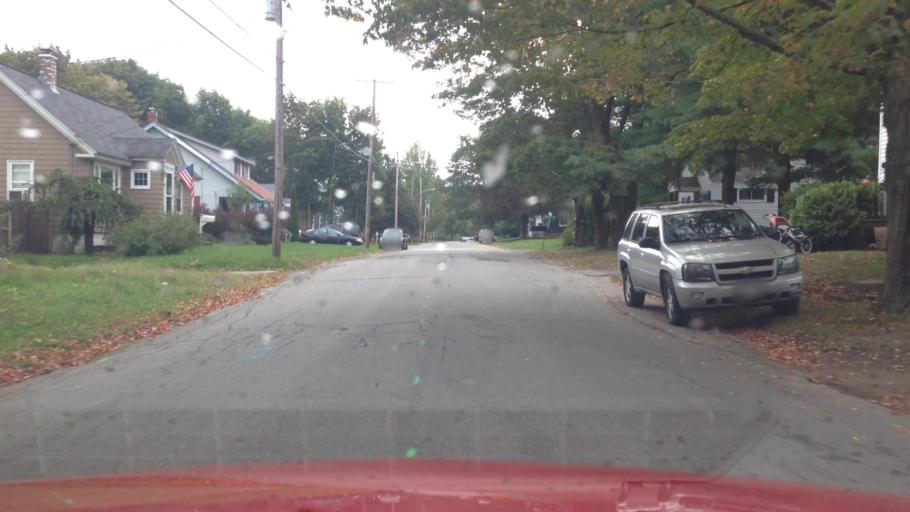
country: US
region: Maine
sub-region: Cumberland County
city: Westbrook
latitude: 43.6757
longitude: -70.3499
